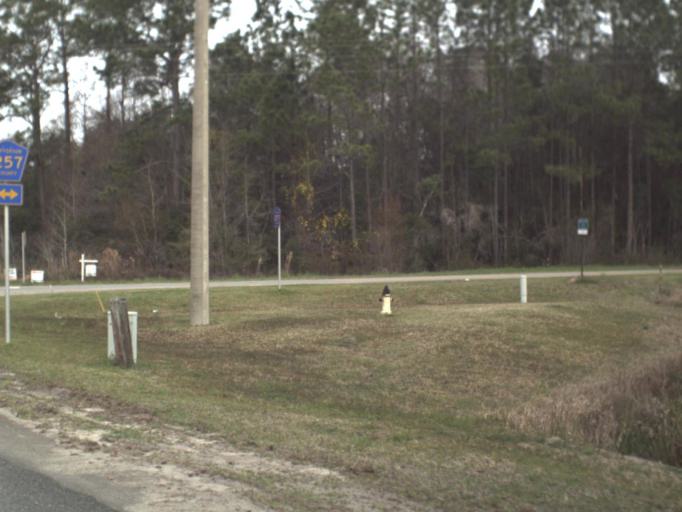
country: US
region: Florida
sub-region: Jefferson County
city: Monticello
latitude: 30.5025
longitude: -83.7589
